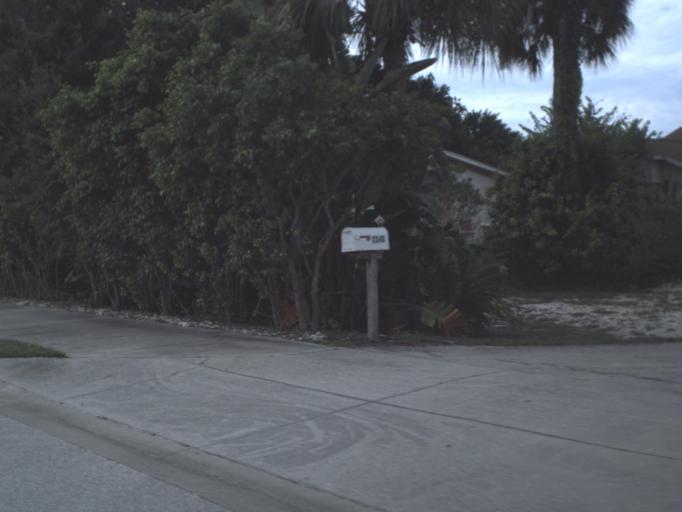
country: US
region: Florida
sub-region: Sarasota County
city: South Venice
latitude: 27.0152
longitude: -82.3856
